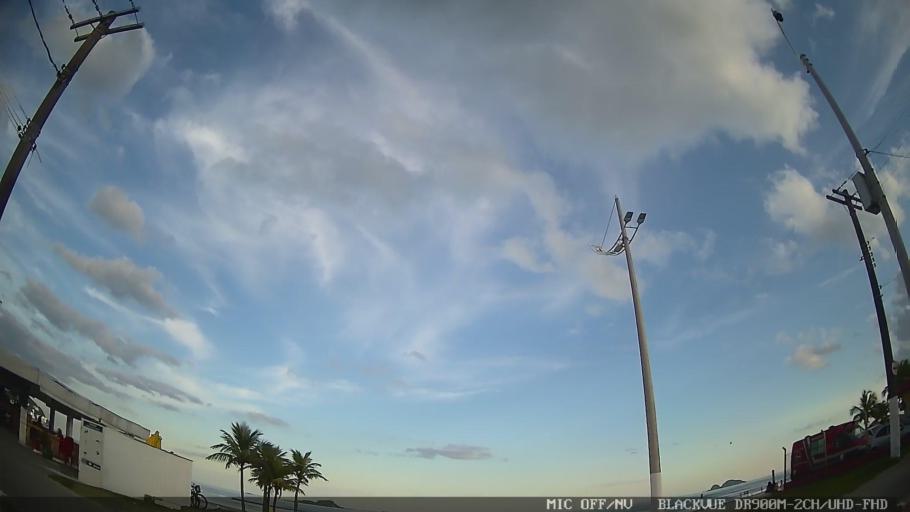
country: BR
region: Sao Paulo
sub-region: Guaruja
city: Guaruja
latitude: -23.9862
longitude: -46.2263
